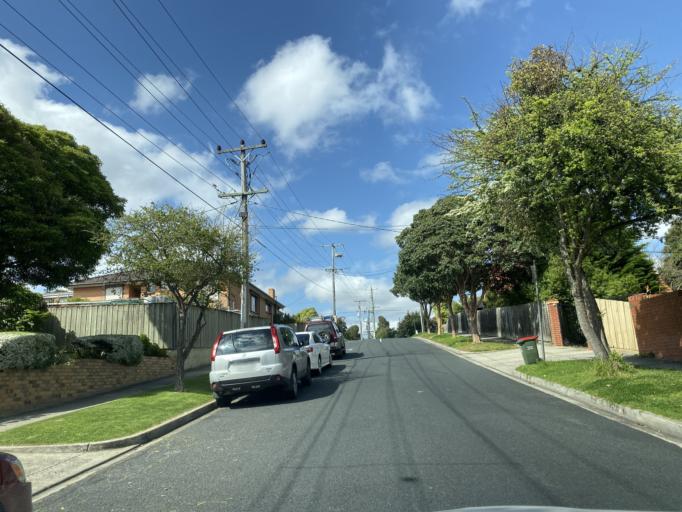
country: AU
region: Victoria
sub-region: Whitehorse
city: Burwood
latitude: -37.8506
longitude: 145.1279
